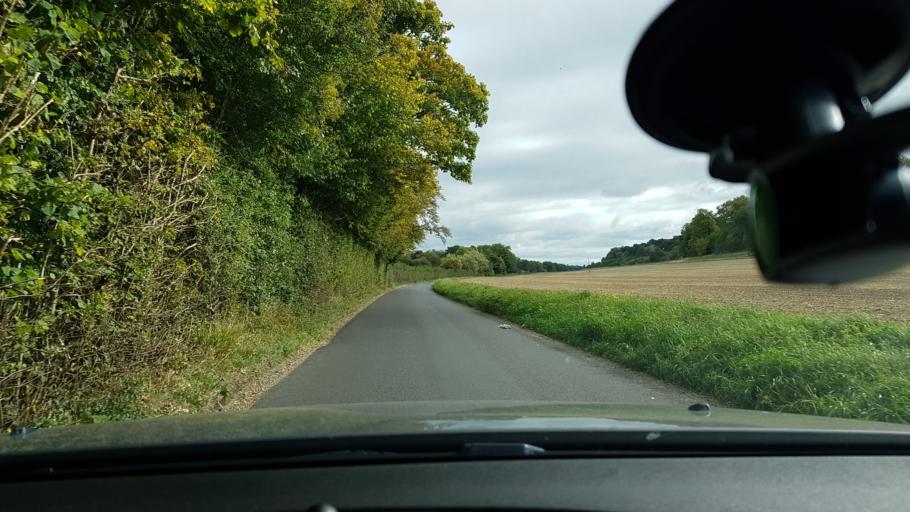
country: GB
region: England
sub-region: Wiltshire
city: Chilton Foliat
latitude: 51.4298
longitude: -1.5512
